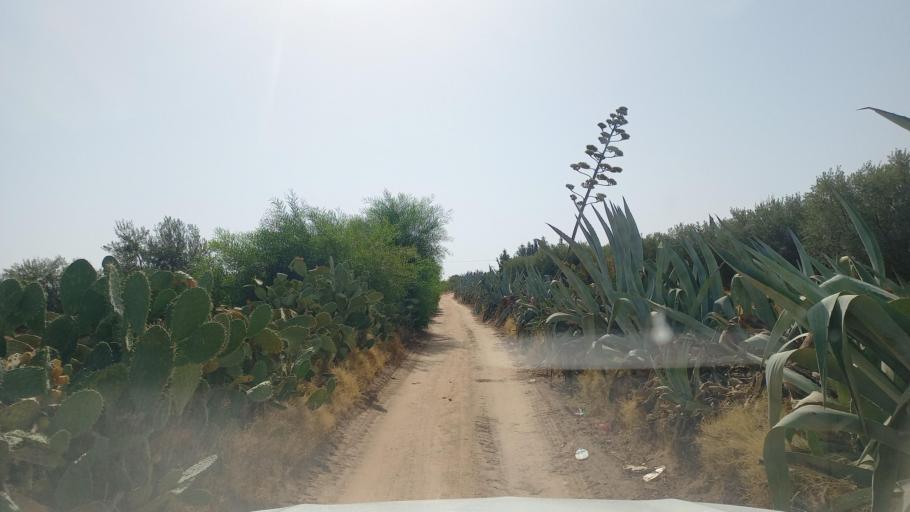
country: TN
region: Al Qasrayn
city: Kasserine
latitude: 35.2391
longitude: 9.0503
